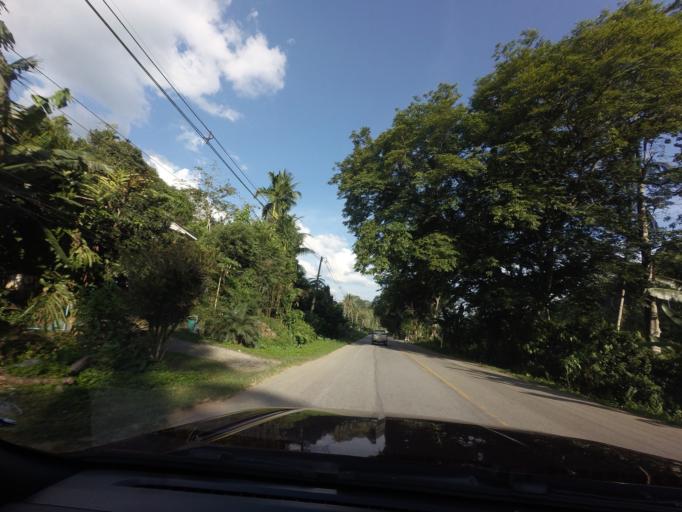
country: TH
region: Yala
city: Than To
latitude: 6.1749
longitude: 101.1769
